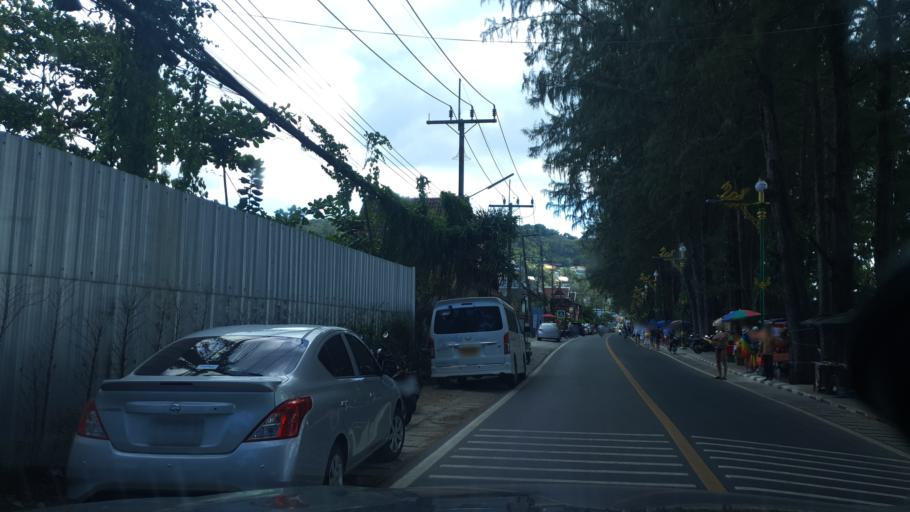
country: TH
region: Phuket
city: Thalang
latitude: 8.0614
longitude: 98.2775
